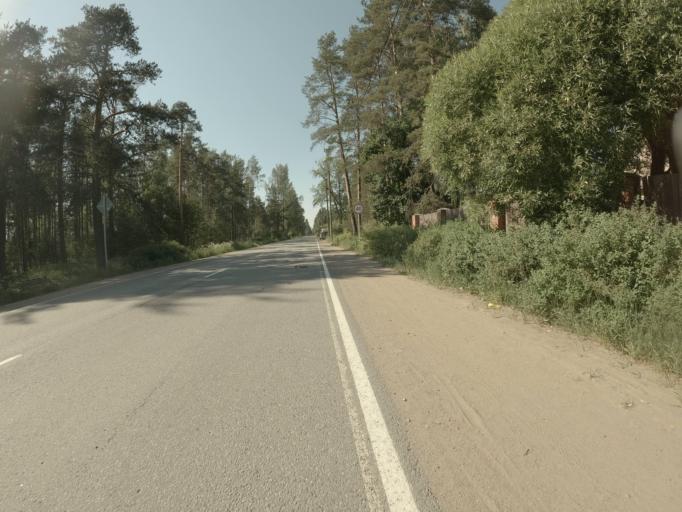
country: RU
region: Leningrad
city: Yakovlevo
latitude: 60.4705
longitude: 29.2840
